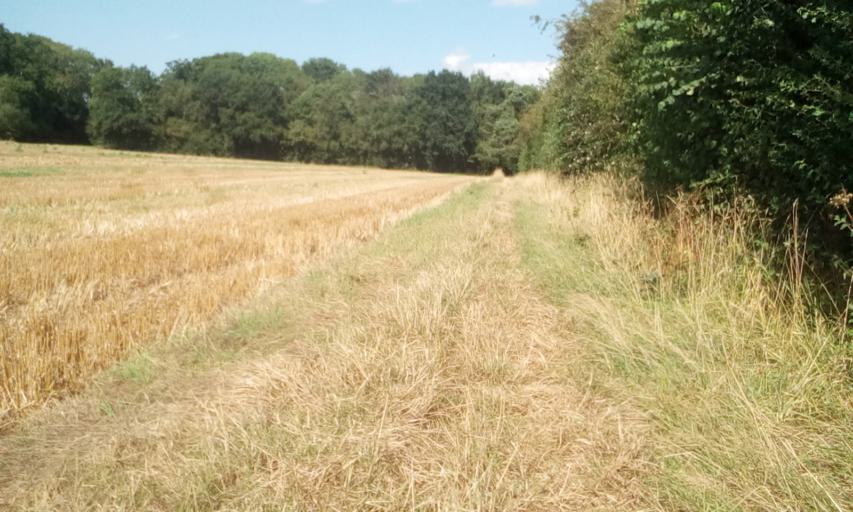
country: FR
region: Lower Normandy
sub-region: Departement du Calvados
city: Argences
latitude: 49.1404
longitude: -0.1116
